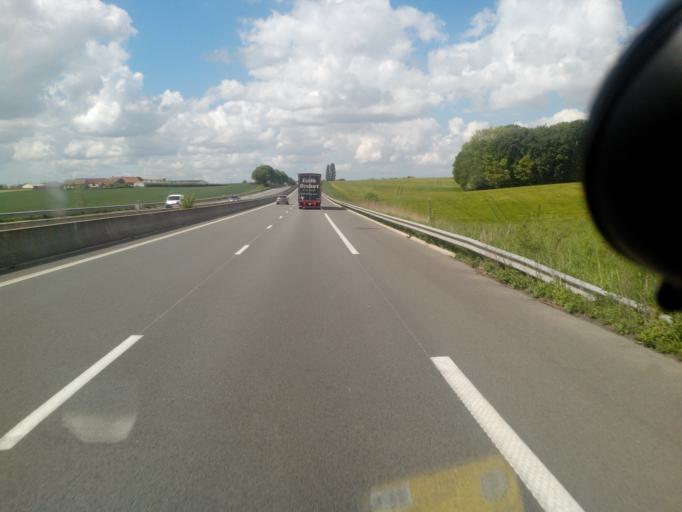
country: FR
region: Nord-Pas-de-Calais
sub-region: Departement du Nord
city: Godewaersvelde
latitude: 50.7732
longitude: 2.6333
